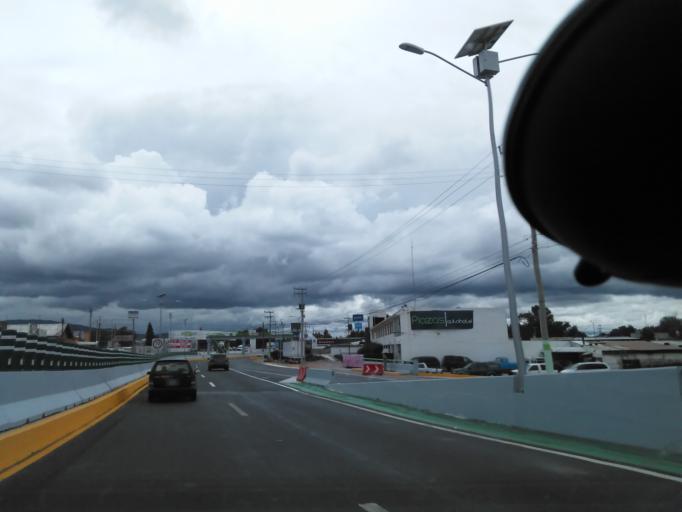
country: MX
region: Hidalgo
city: El Llano
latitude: 20.0536
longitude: -99.3124
